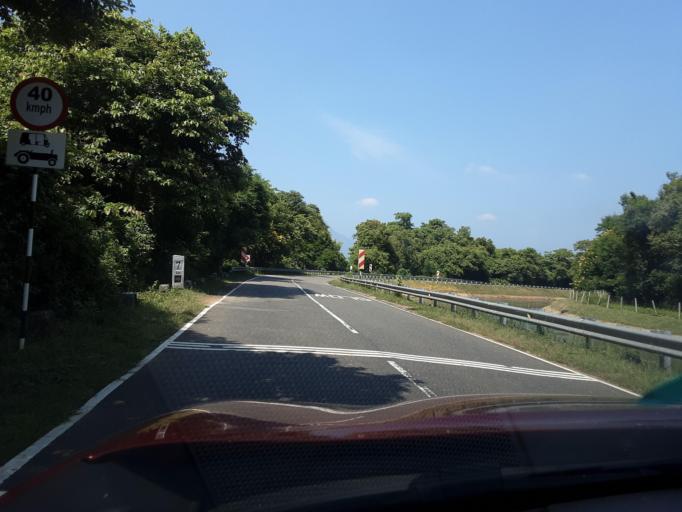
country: LK
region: Uva
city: Badulla
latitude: 7.2735
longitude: 81.0469
